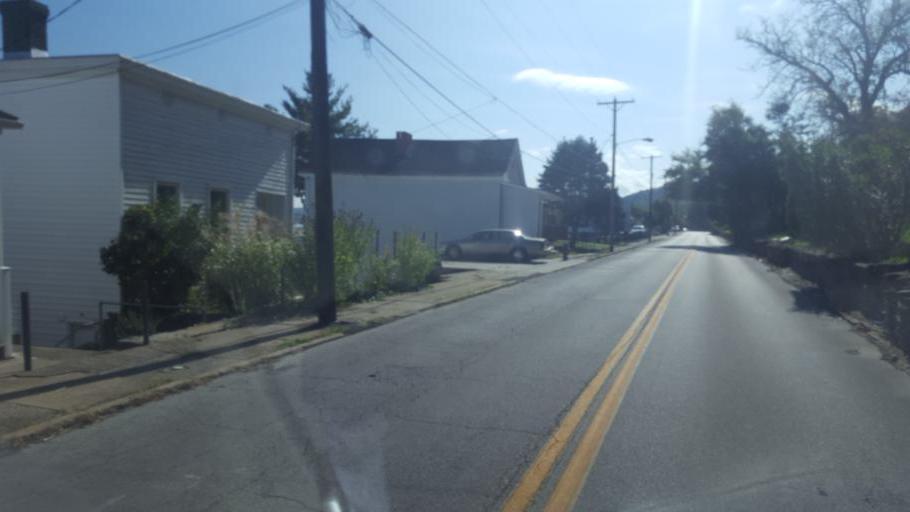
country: US
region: Ohio
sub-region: Brown County
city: Aberdeen
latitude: 38.6560
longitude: -83.7756
